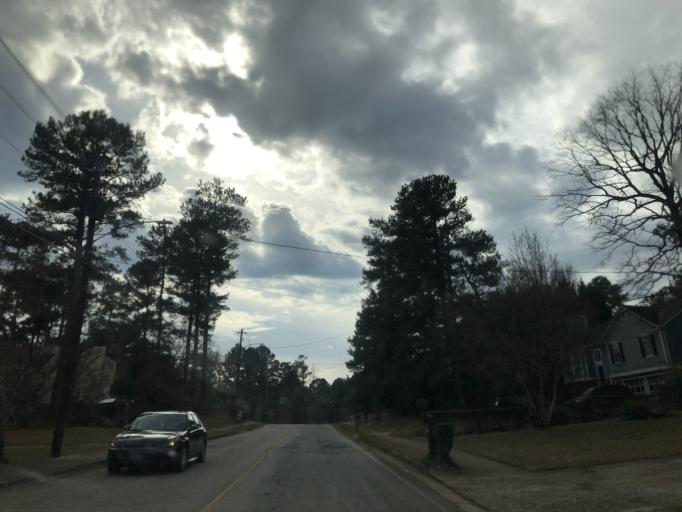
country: US
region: Georgia
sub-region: DeKalb County
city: Panthersville
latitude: 33.6740
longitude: -84.2148
